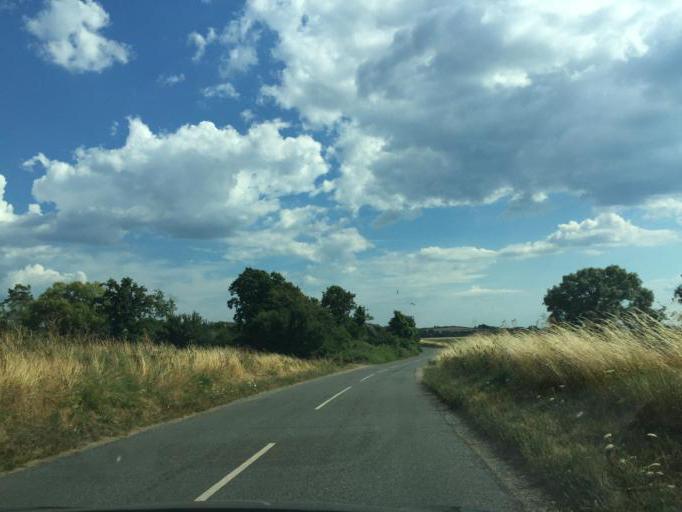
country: DK
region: South Denmark
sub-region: Assens Kommune
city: Assens
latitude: 55.1697
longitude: 9.9856
